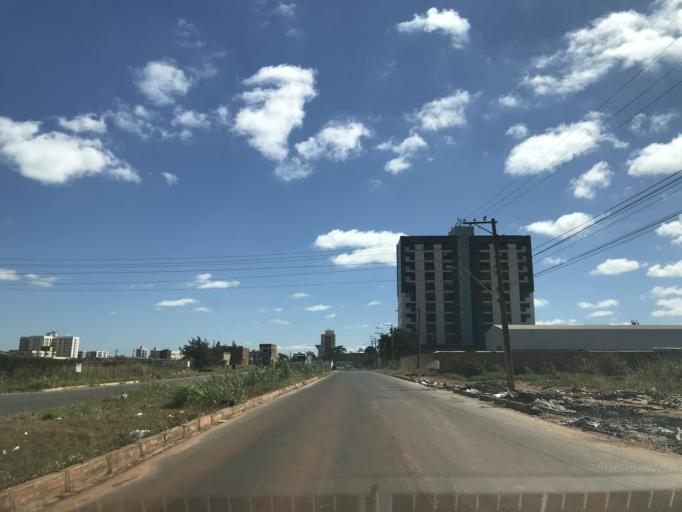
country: BR
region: Federal District
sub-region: Brasilia
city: Brasilia
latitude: -15.8738
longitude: -48.0251
